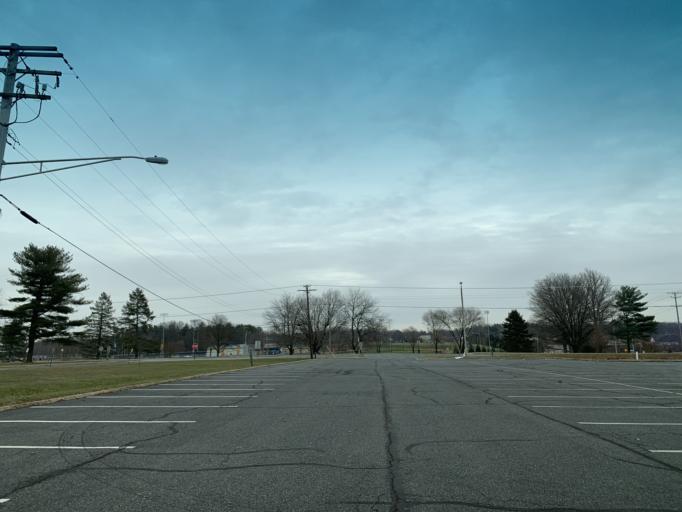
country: US
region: Maryland
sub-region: Harford County
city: South Bel Air
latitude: 39.5559
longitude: -76.2874
